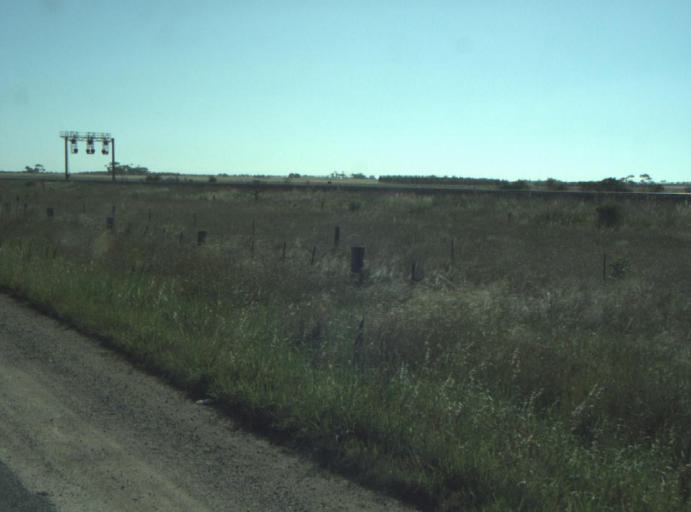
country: AU
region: Victoria
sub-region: Greater Geelong
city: Lara
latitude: -37.9949
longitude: 144.4493
